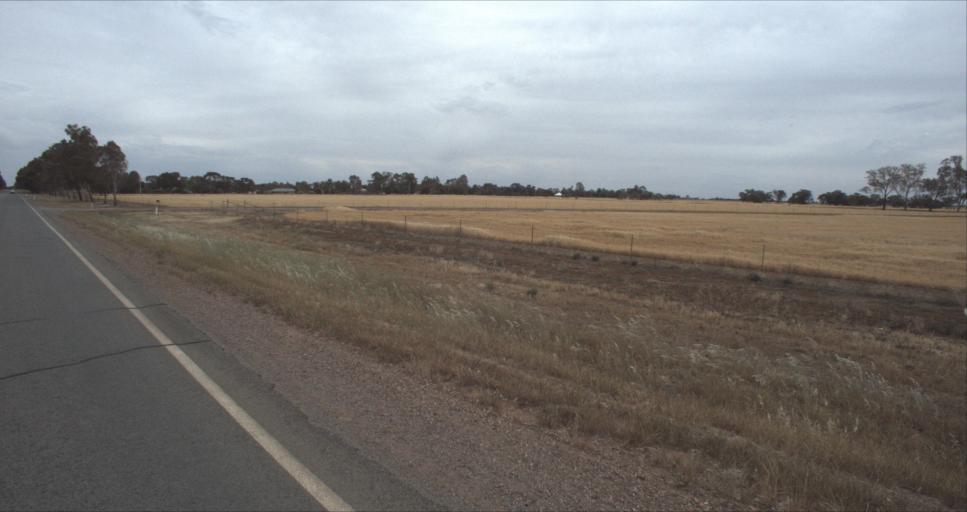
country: AU
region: New South Wales
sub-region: Leeton
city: Leeton
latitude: -34.5166
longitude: 146.4168
